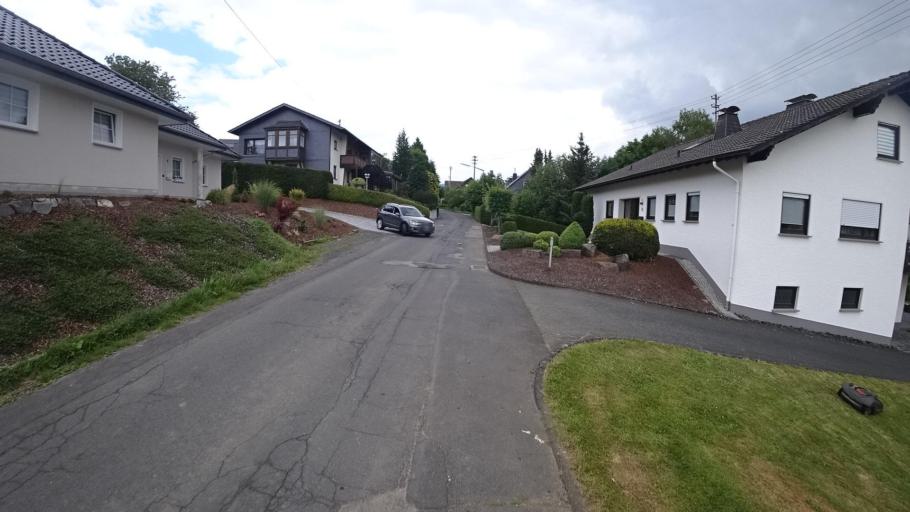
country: DE
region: Rheinland-Pfalz
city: Eichelhardt
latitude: 50.7188
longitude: 7.6943
